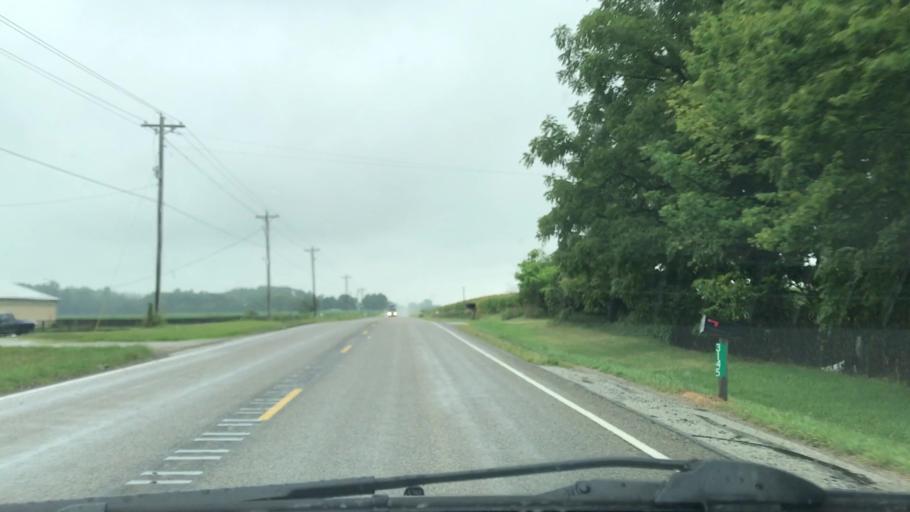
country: US
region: Indiana
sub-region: Boone County
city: Lebanon
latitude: 40.1266
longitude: -86.4098
